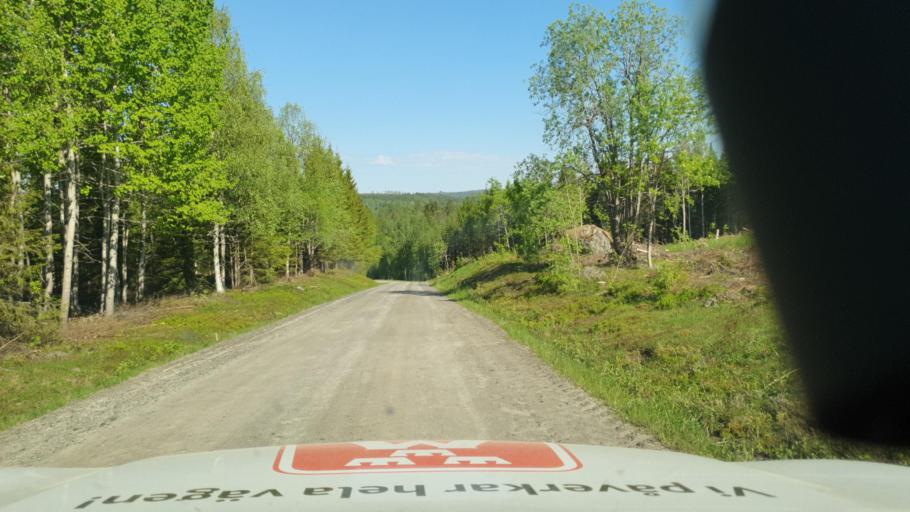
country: SE
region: Vaesterbotten
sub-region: Vannas Kommun
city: Vannasby
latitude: 64.0187
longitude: 19.7622
